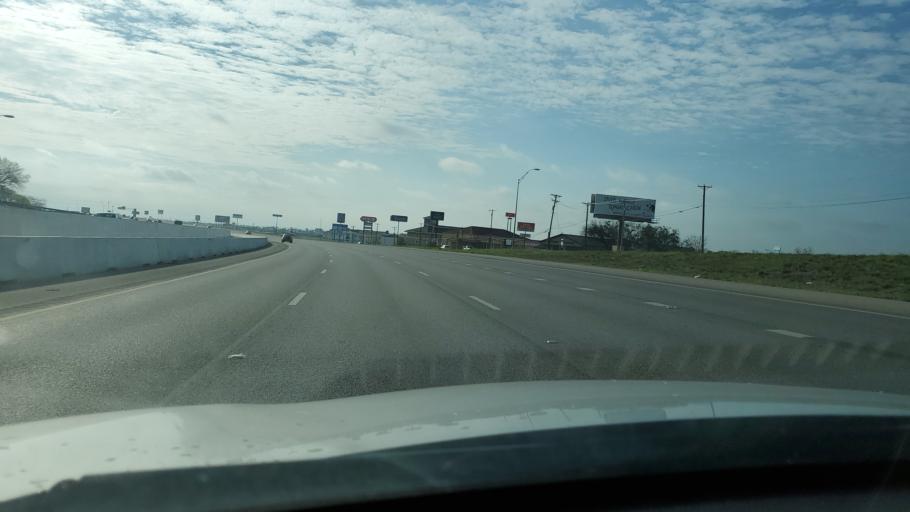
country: US
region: Texas
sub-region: Bell County
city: Killeen
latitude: 31.0976
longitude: -97.7384
